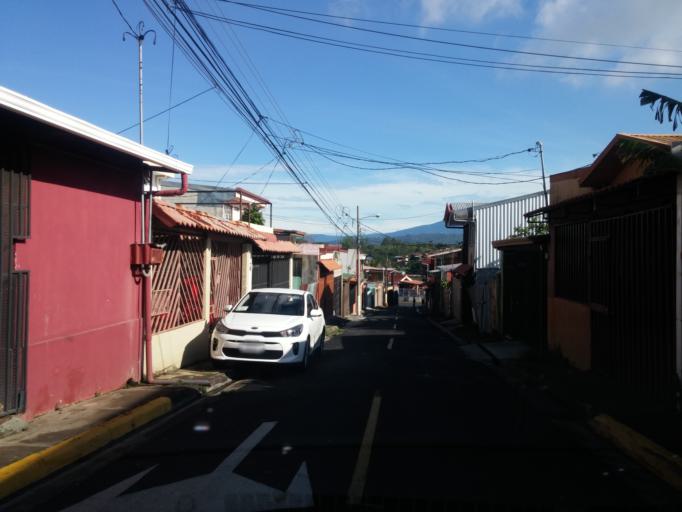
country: CR
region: Heredia
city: Mercedes
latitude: 10.0040
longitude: -84.1424
